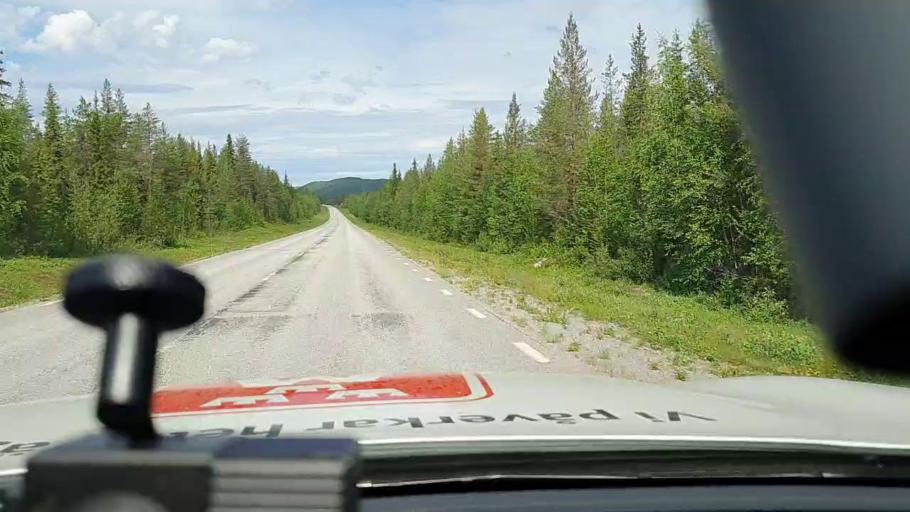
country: SE
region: Norrbotten
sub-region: Jokkmokks Kommun
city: Jokkmokk
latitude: 66.5469
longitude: 20.1309
